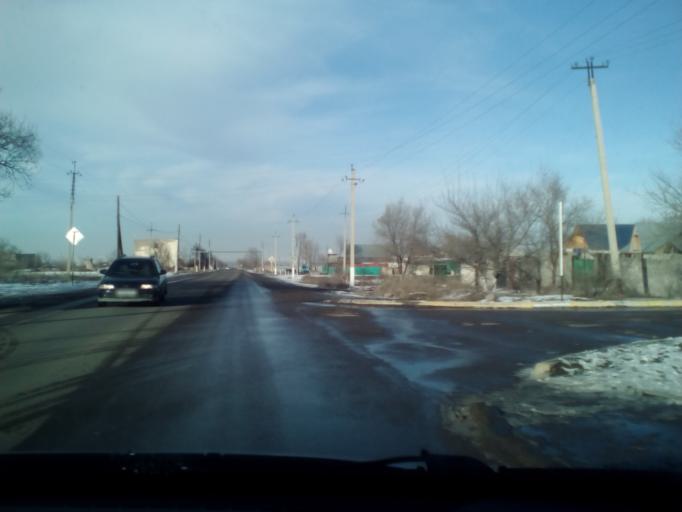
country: KZ
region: Almaty Oblysy
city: Burunday
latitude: 43.1898
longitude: 76.4148
